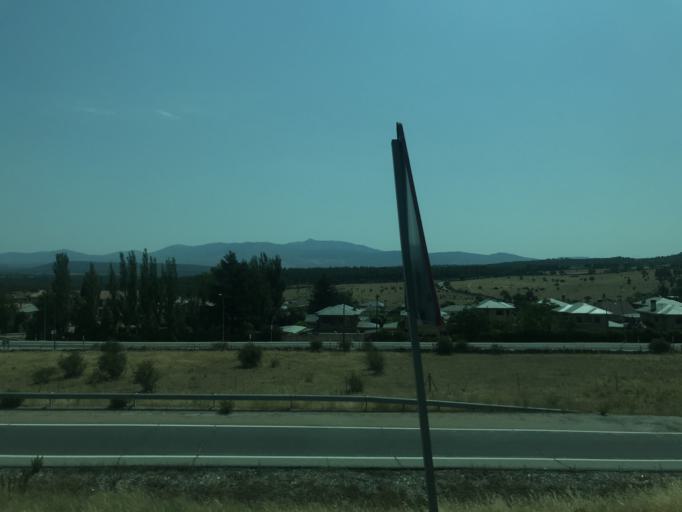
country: ES
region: Madrid
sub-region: Provincia de Madrid
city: Buitrago del Lozoya
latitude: 40.9816
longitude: -3.6386
